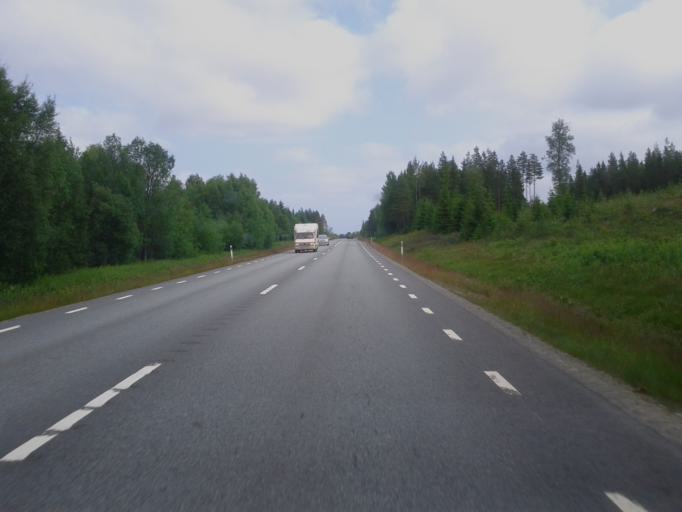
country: SE
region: Vaesterbotten
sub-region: Skelleftea Kommun
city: Burea
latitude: 64.3406
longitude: 21.2783
